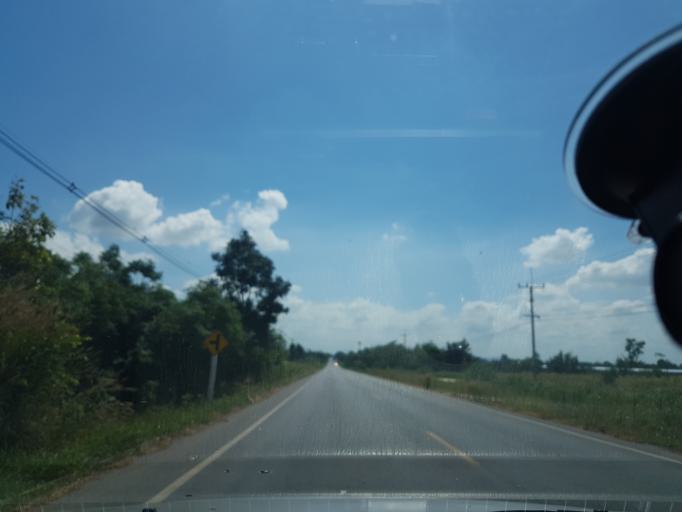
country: TH
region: Lop Buri
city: Phatthana Nikhom
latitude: 14.9442
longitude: 101.0094
